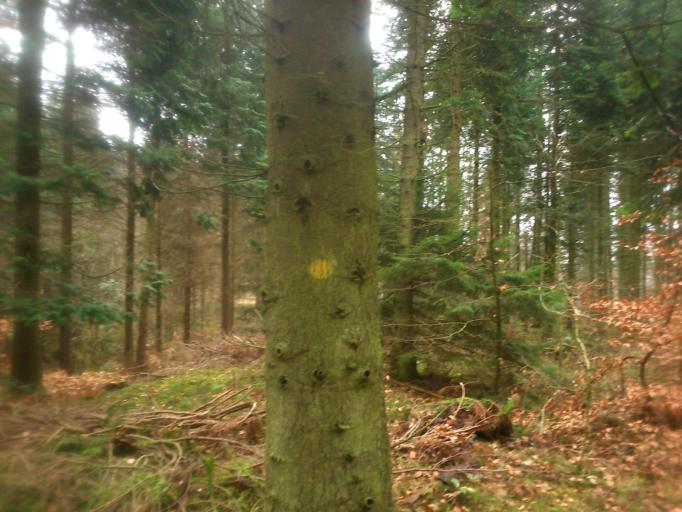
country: DK
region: Central Jutland
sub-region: Viborg Kommune
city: Bjerringbro
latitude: 56.3878
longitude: 9.7119
